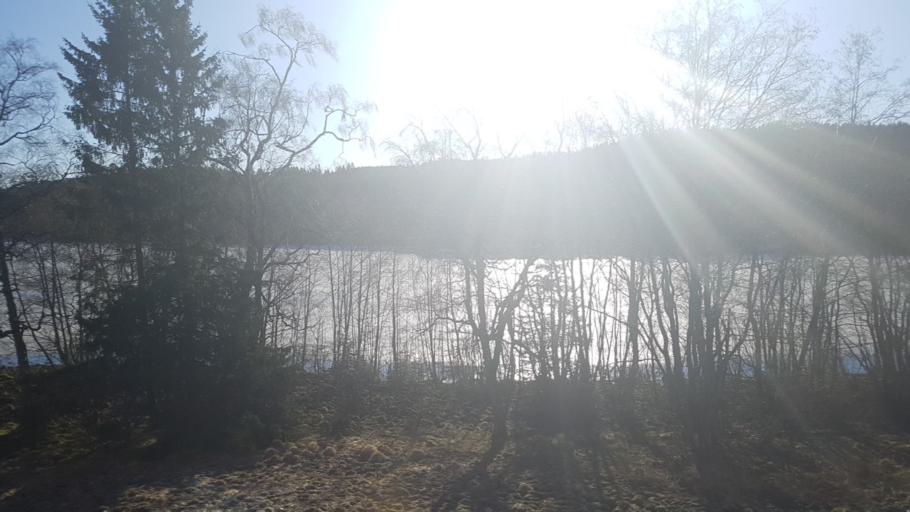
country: NO
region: Nord-Trondelag
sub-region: Levanger
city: Skogn
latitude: 63.6663
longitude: 11.1062
